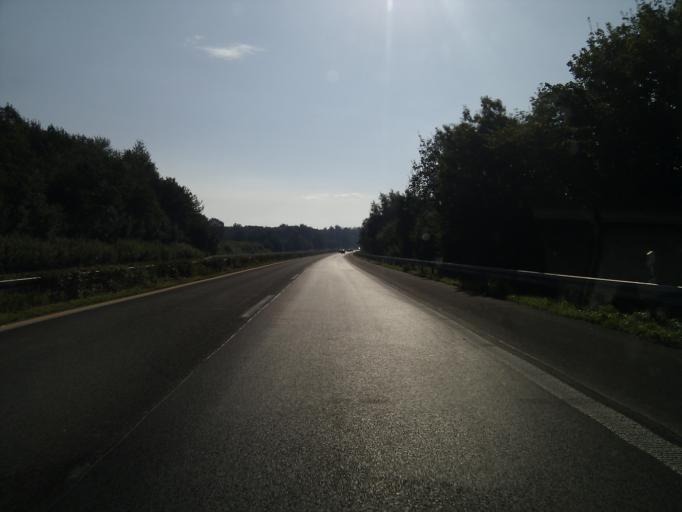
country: DE
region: North Rhine-Westphalia
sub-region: Regierungsbezirk Dusseldorf
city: Uedem
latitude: 51.6470
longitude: 6.2575
